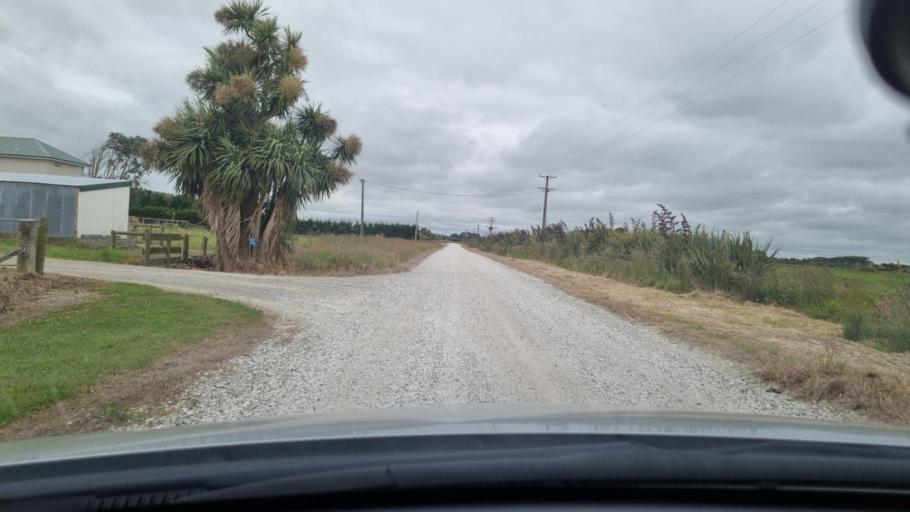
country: NZ
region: Southland
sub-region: Invercargill City
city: Invercargill
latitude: -46.3833
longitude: 168.2845
